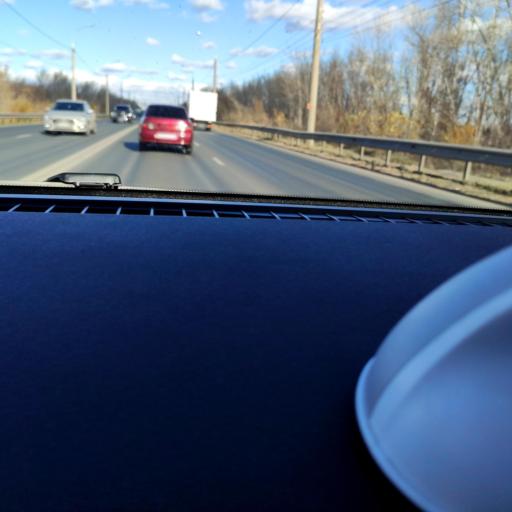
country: RU
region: Samara
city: Samara
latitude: 53.1467
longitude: 50.1835
